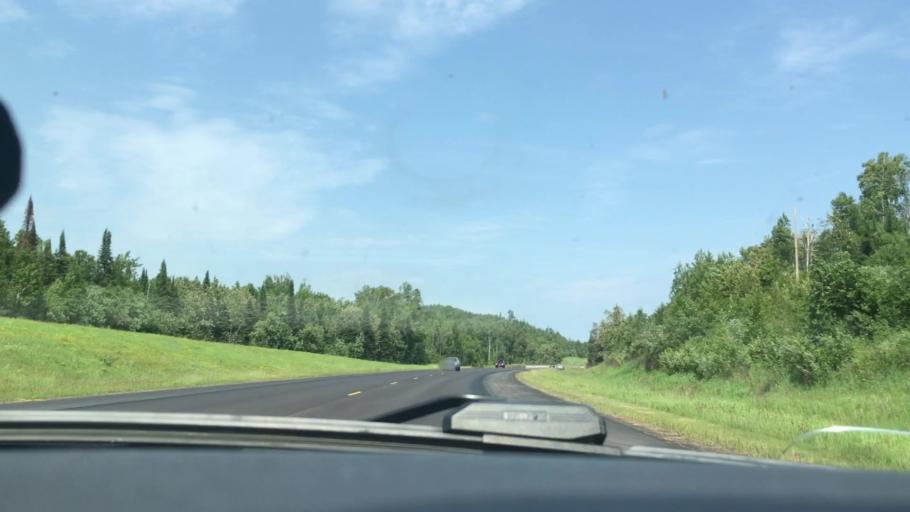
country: US
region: Minnesota
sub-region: Lake County
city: Silver Bay
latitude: 47.3349
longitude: -91.2037
